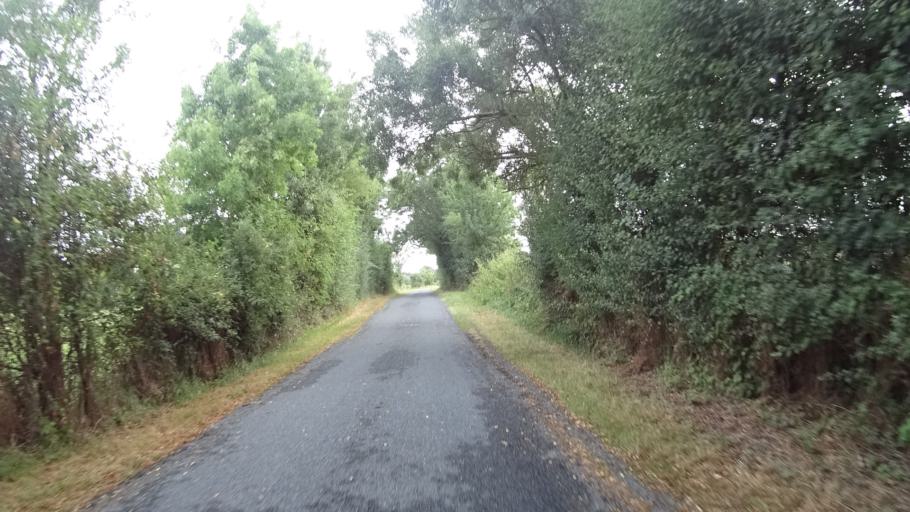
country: FR
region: Pays de la Loire
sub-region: Departement de la Loire-Atlantique
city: Anetz
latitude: 47.3643
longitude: -1.0909
